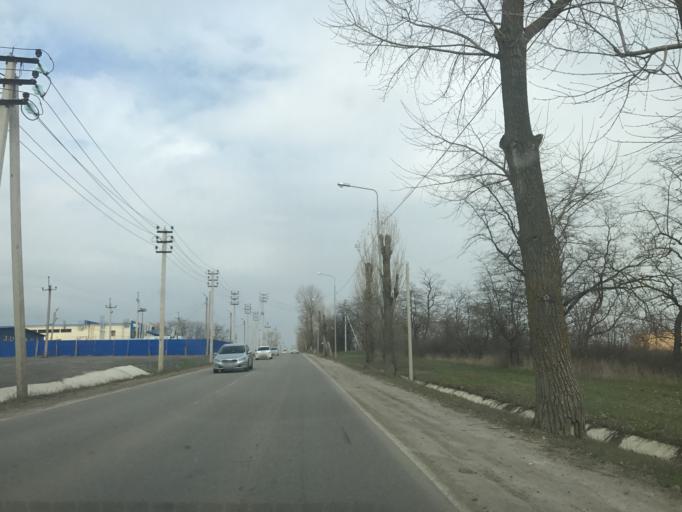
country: RU
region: Rostov
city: Aksay
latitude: 47.3017
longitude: 39.9302
